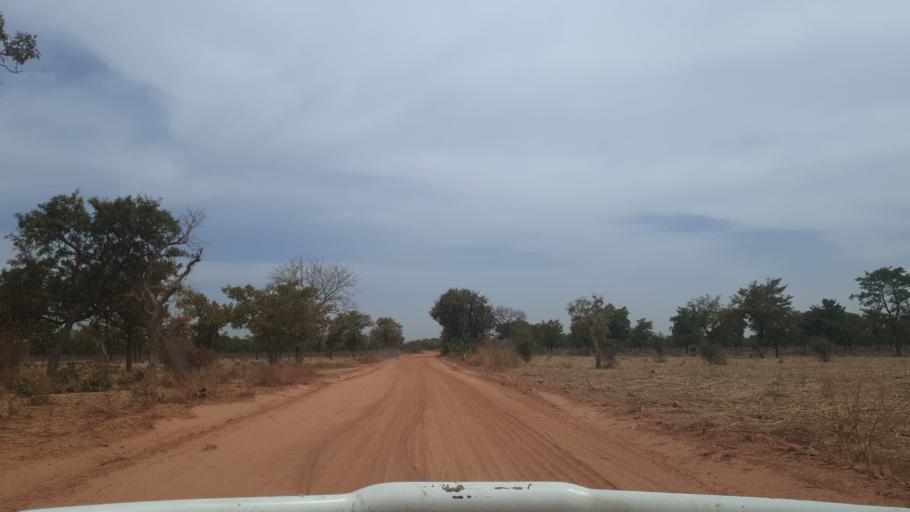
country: ML
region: Sikasso
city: Yorosso
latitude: 12.2203
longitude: -4.7546
